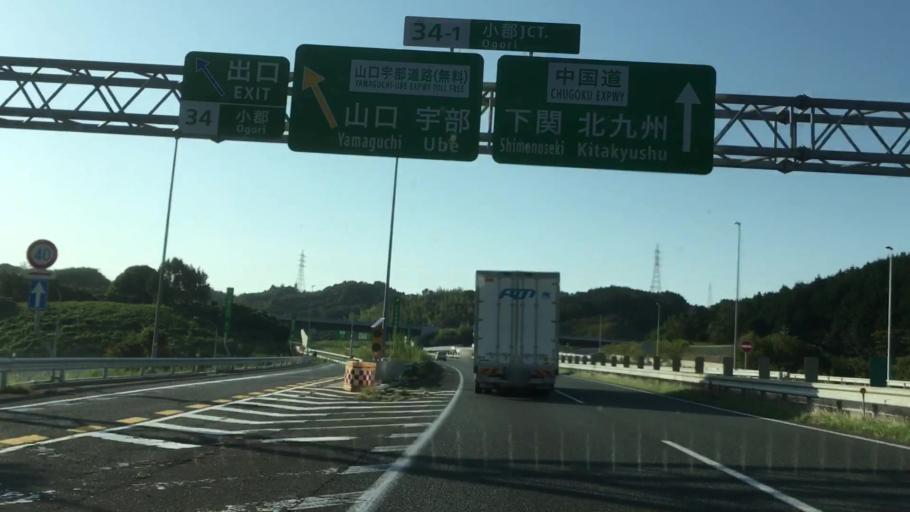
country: JP
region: Yamaguchi
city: Ogori-shimogo
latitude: 34.1253
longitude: 131.4065
